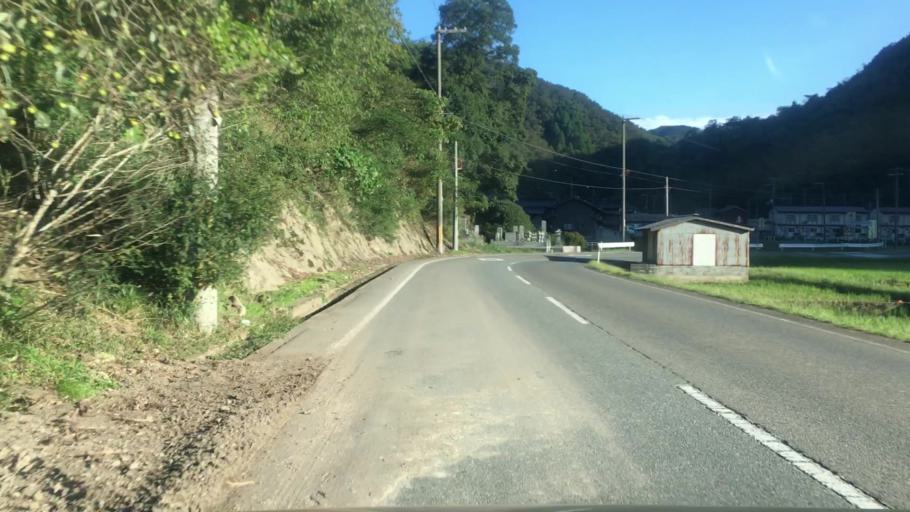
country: JP
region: Hyogo
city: Toyooka
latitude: 35.6066
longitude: 134.8077
